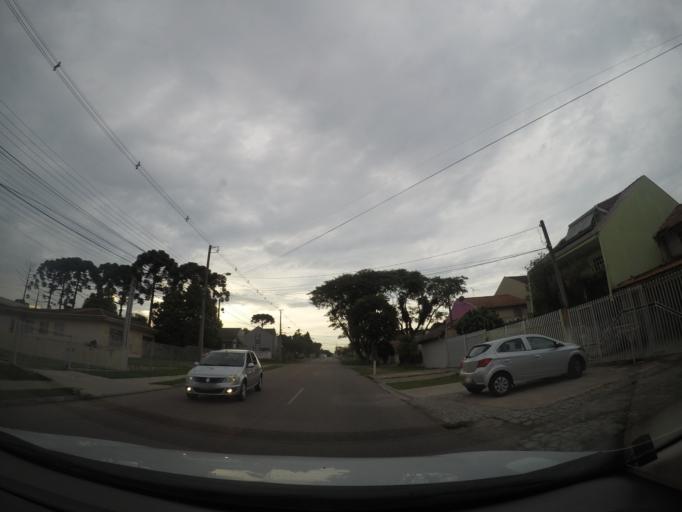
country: BR
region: Parana
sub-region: Sao Jose Dos Pinhais
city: Sao Jose dos Pinhais
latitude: -25.5173
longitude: -49.2381
